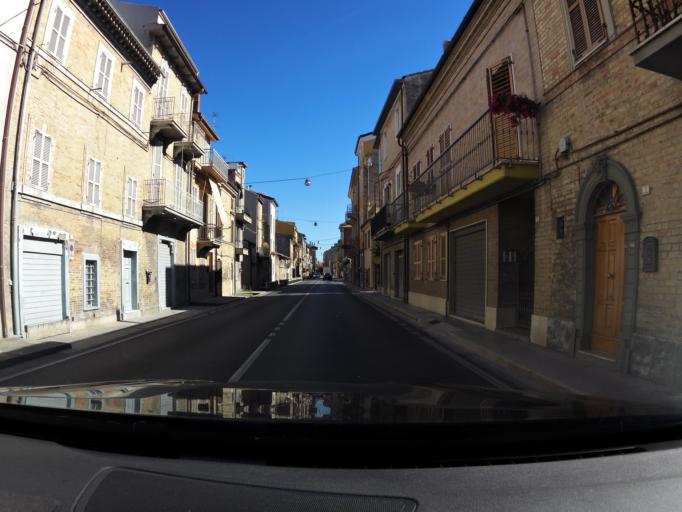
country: IT
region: The Marches
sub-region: Province of Fermo
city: Porto San Giorgio
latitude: 43.1828
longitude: 13.7922
